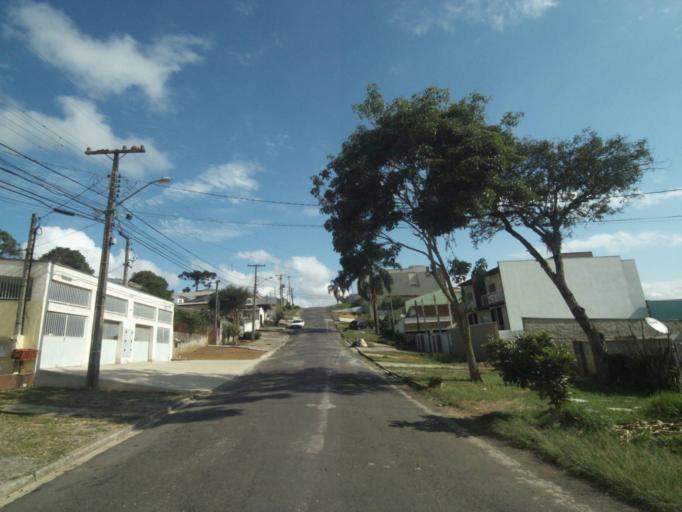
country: BR
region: Parana
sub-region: Curitiba
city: Curitiba
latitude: -25.3890
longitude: -49.3012
